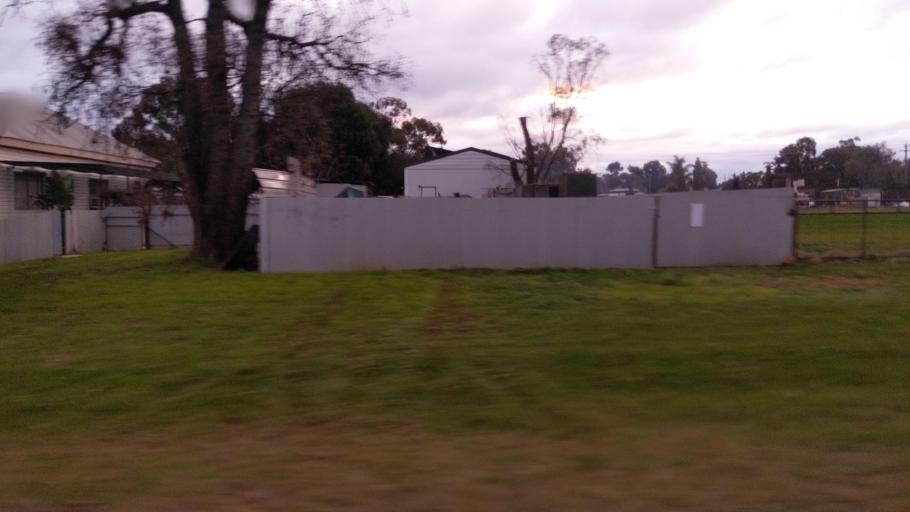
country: AU
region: New South Wales
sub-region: Narrandera
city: Narrandera
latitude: -34.7350
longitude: 146.7835
